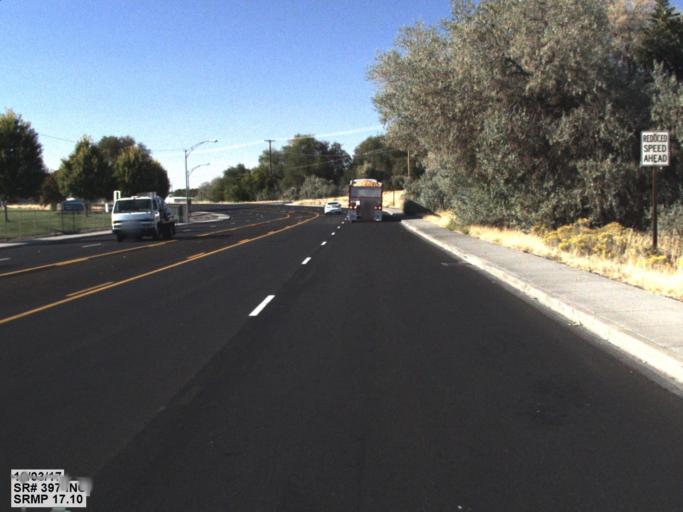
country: US
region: Washington
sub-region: Franklin County
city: Pasco
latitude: 46.2040
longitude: -119.0992
